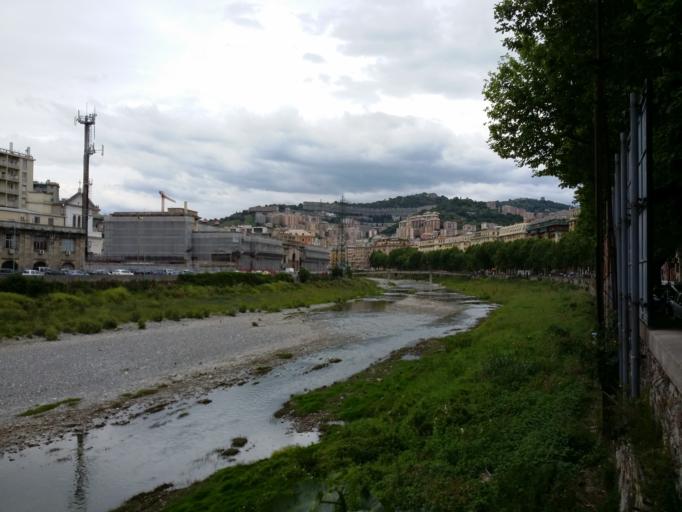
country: IT
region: Liguria
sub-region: Provincia di Genova
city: Genoa
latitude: 44.4080
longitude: 8.9516
